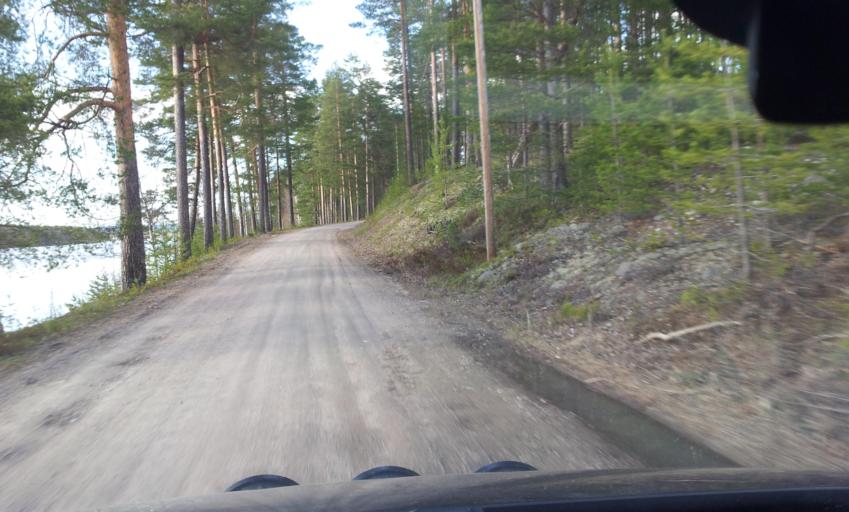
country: SE
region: Vaesternorrland
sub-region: Ange Kommun
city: Ange
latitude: 62.1487
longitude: 15.6722
